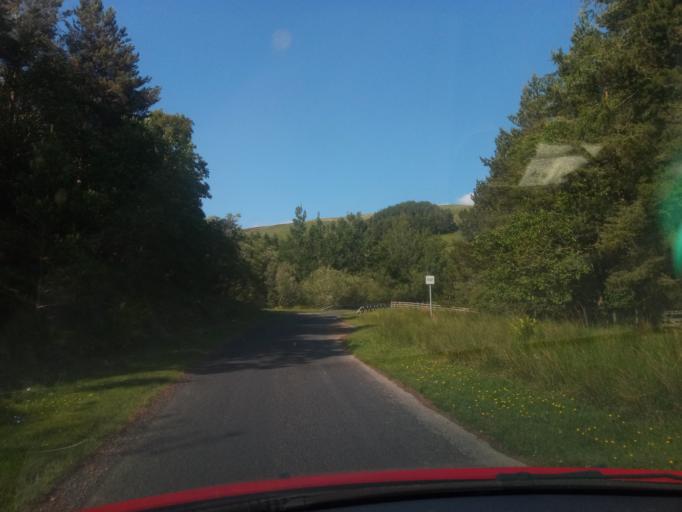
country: GB
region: Scotland
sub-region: The Scottish Borders
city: Peebles
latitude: 55.4971
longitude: -3.2590
